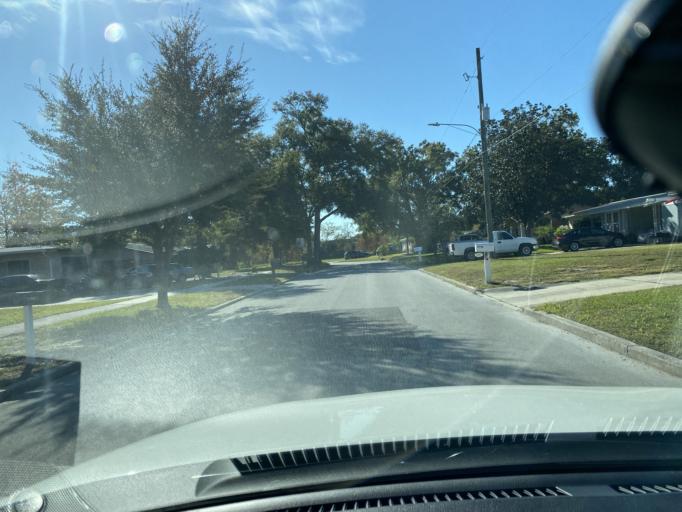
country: US
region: Florida
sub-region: Orange County
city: Azalea Park
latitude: 28.5280
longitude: -81.3172
